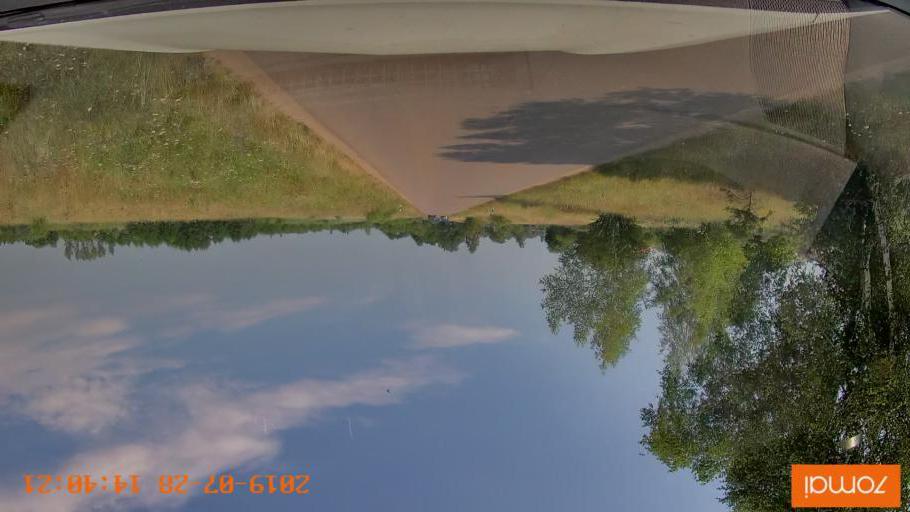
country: RU
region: Kaliningrad
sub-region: Gorod Kaliningrad
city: Yantarnyy
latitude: 54.8511
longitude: 19.9588
